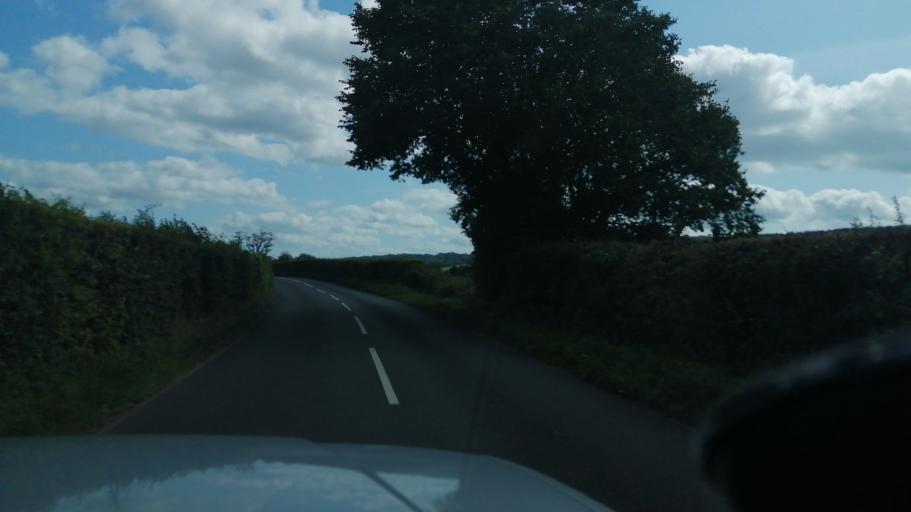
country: GB
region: England
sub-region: Herefordshire
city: Blakemere
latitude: 52.0708
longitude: -2.9336
